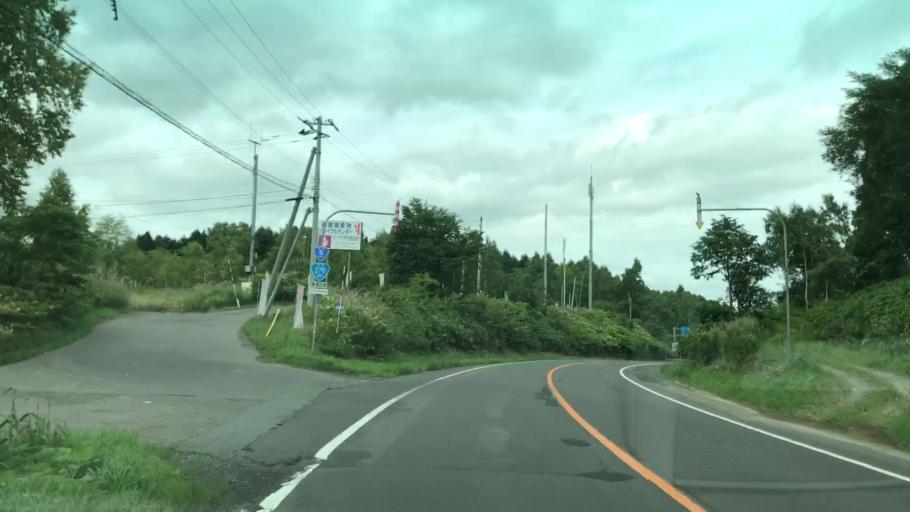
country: JP
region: Hokkaido
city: Niseko Town
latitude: 42.9227
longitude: 140.7188
